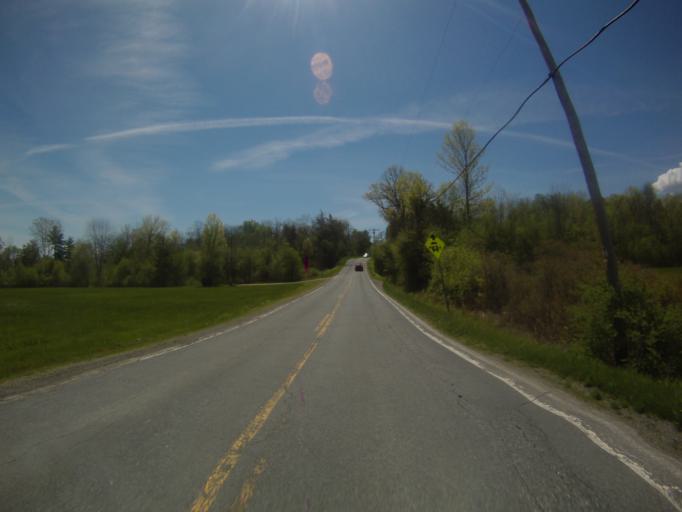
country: US
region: New York
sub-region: Essex County
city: Port Henry
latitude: 43.9824
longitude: -73.4224
